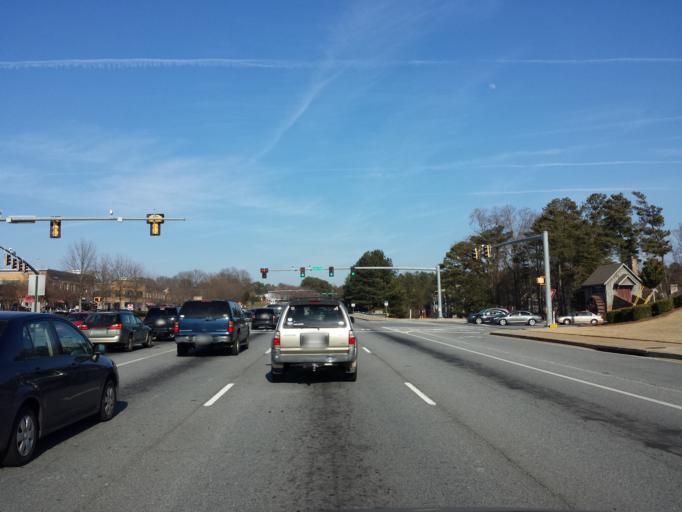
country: US
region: Georgia
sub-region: Cobb County
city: Kennesaw
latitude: 34.0359
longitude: -84.5704
